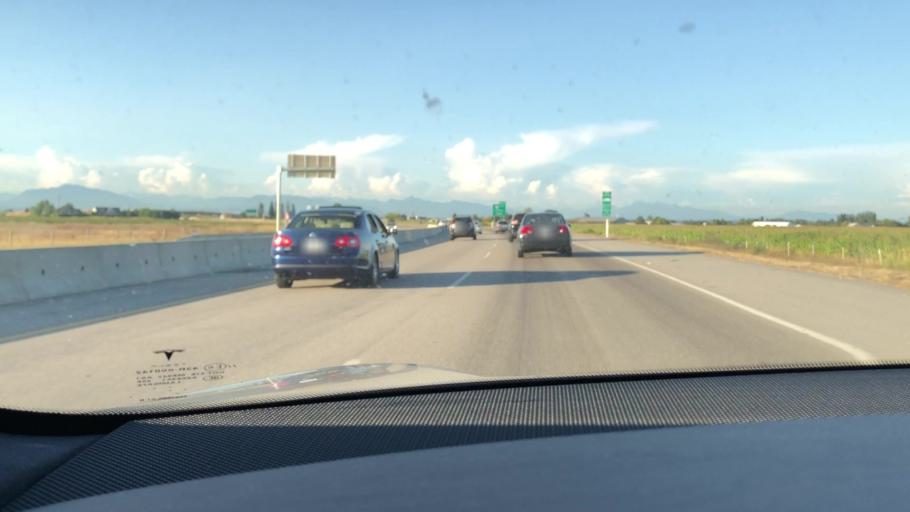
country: CA
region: British Columbia
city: Ladner
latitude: 49.0462
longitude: -123.0614
